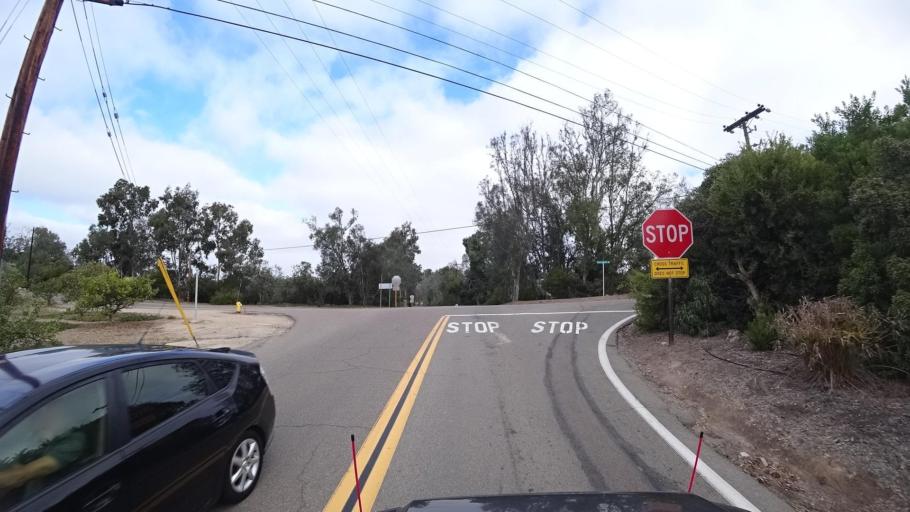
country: US
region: California
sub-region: San Diego County
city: Rancho Santa Fe
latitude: 33.0004
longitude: -117.2259
